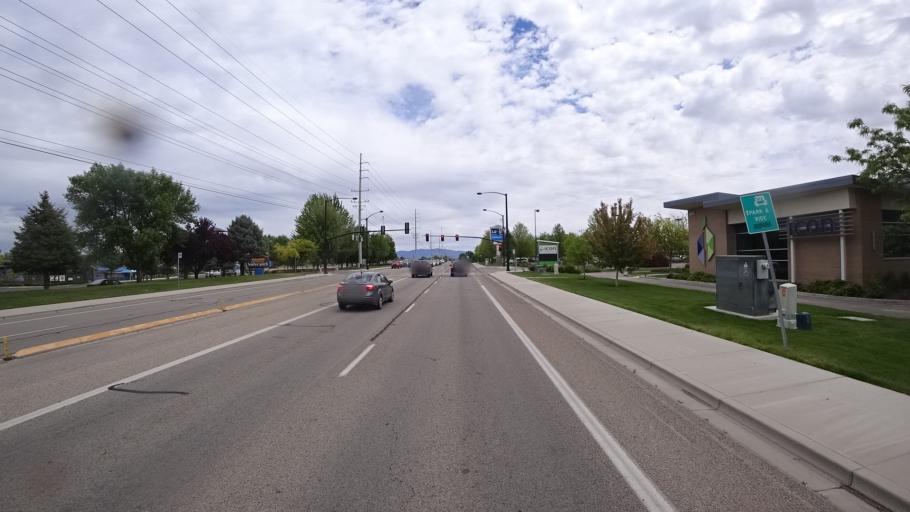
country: US
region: Idaho
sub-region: Ada County
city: Meridian
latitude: 43.5900
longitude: -116.3994
